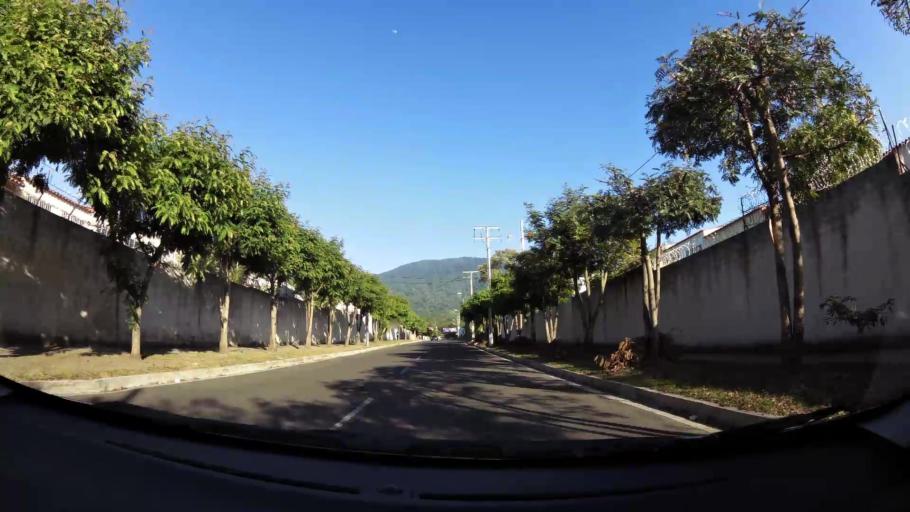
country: SV
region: La Libertad
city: Santa Tecla
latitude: 13.7386
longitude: -89.3527
